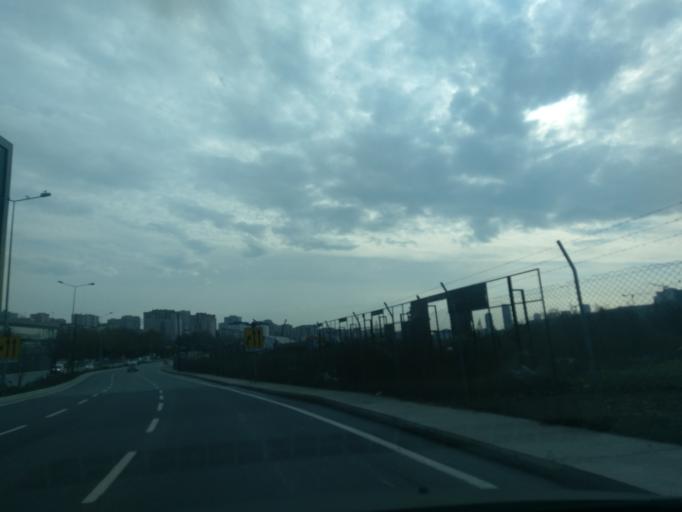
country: TR
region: Istanbul
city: Basaksehir
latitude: 41.0605
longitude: 28.7732
